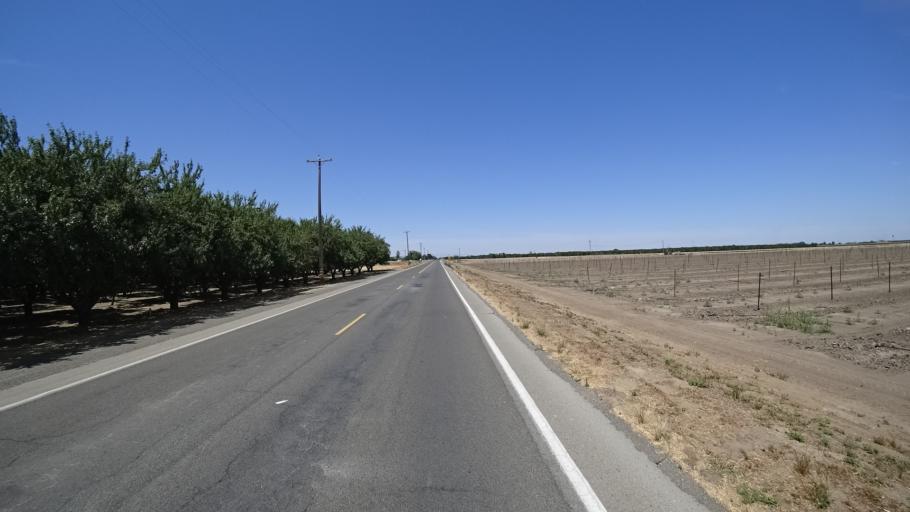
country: US
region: California
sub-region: Kings County
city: Armona
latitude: 36.3426
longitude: -119.7505
